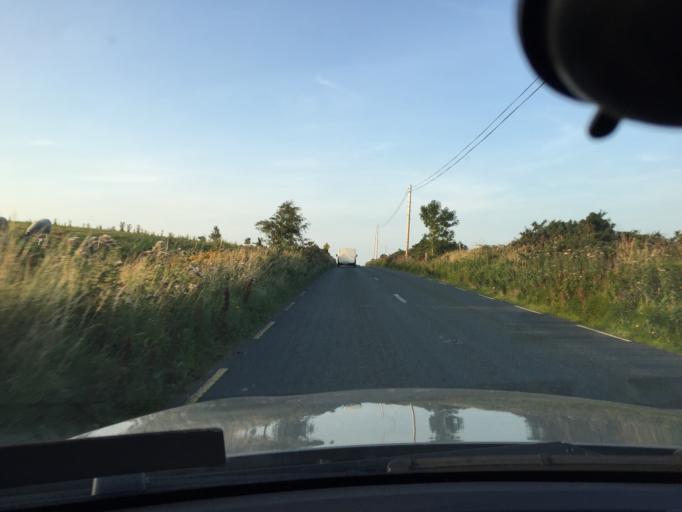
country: IE
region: Leinster
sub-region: Wicklow
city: Kilmacanoge
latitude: 53.1352
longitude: -6.1762
